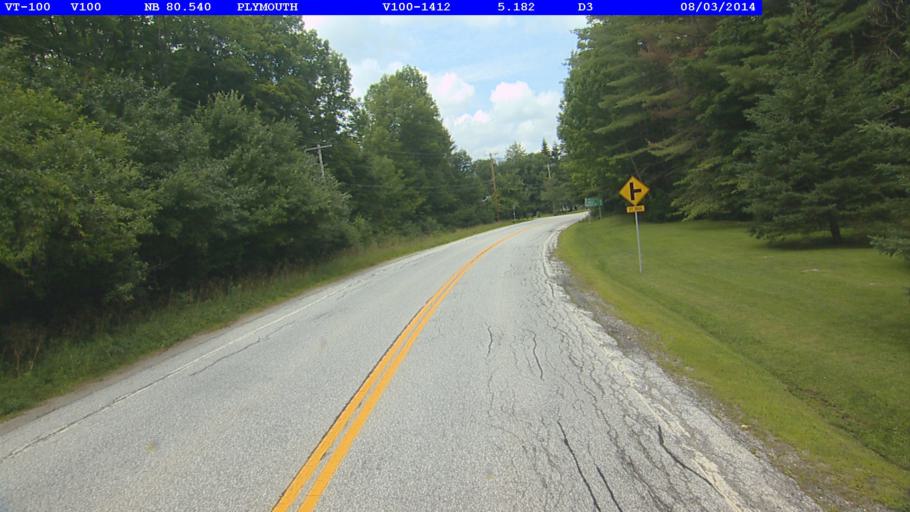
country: US
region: Vermont
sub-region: Windsor County
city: Woodstock
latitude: 43.5282
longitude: -72.7380
